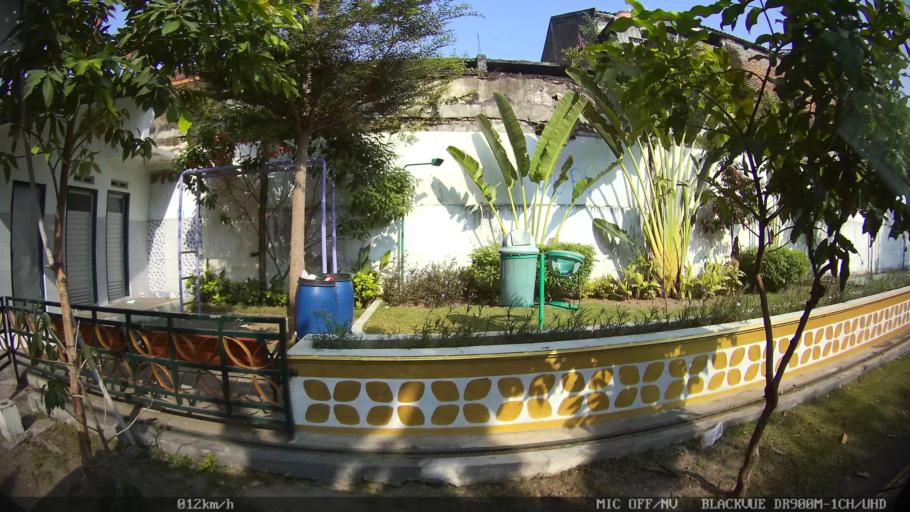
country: ID
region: Daerah Istimewa Yogyakarta
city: Yogyakarta
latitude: -7.8057
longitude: 110.3564
